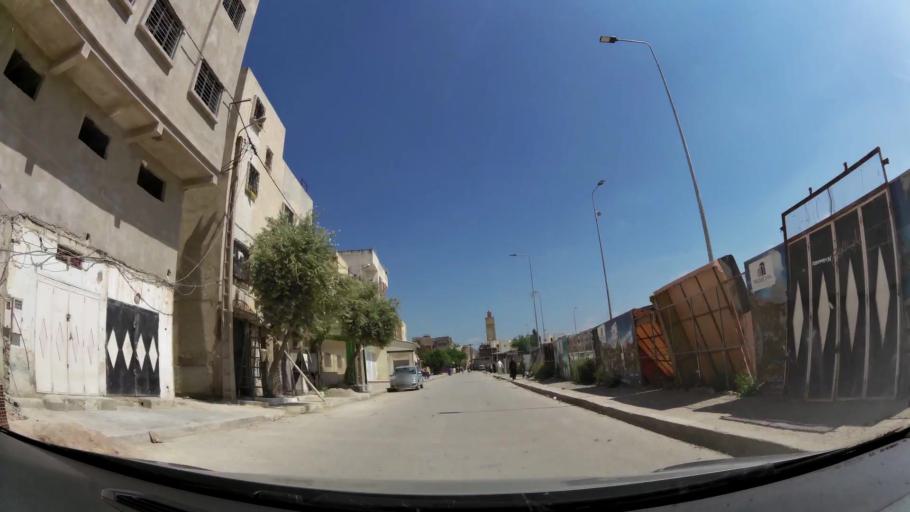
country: MA
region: Fes-Boulemane
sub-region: Fes
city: Fes
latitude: 34.0148
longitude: -5.0312
